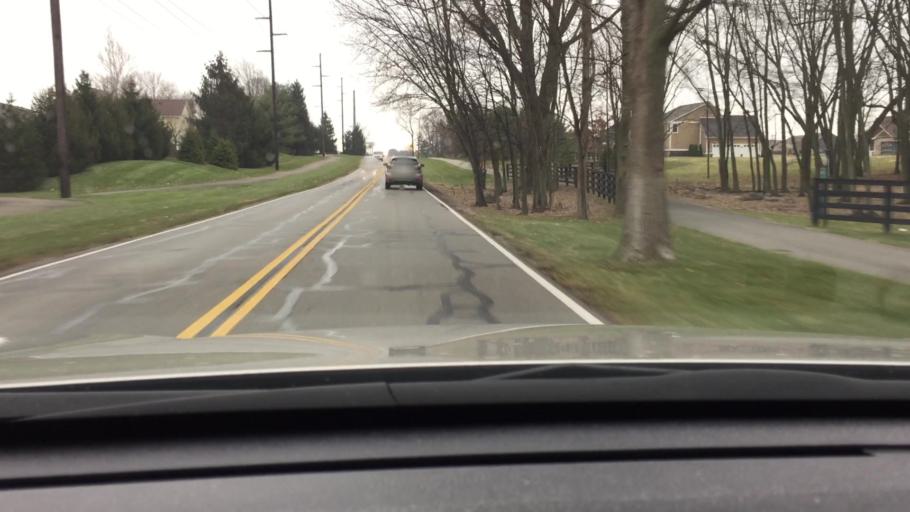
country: US
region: Indiana
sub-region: Hamilton County
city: Carmel
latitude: 40.0076
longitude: -86.1029
